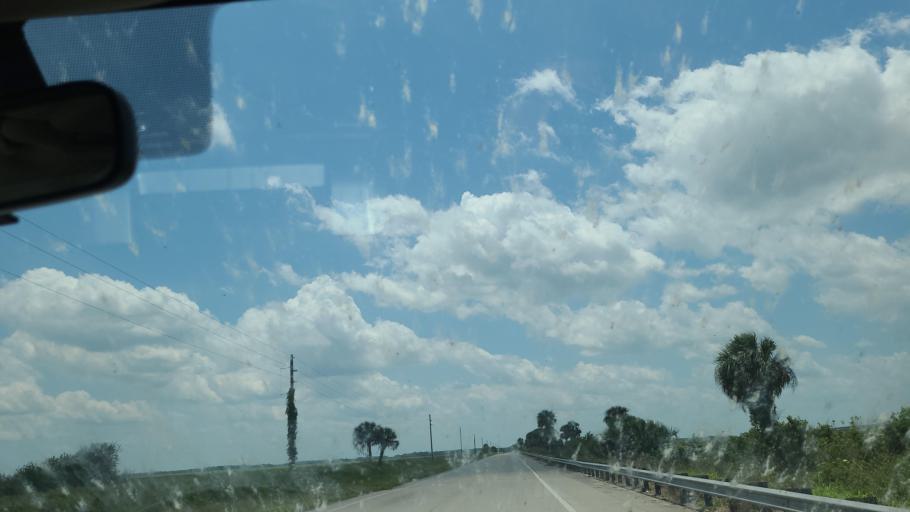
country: US
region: Florida
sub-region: Glades County
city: Buckhead Ridge
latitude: 27.1686
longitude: -81.0935
